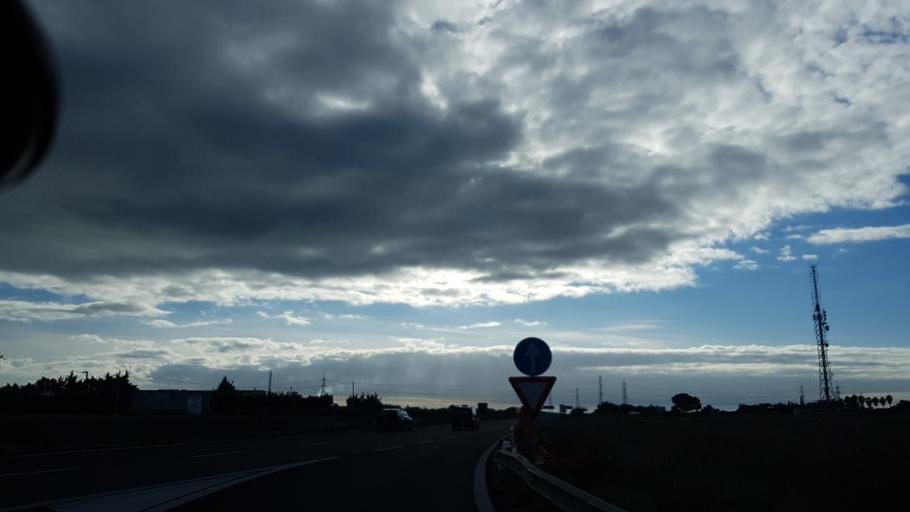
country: IT
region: Apulia
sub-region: Provincia di Brindisi
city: La Rosa
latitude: 40.6134
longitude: 17.9590
